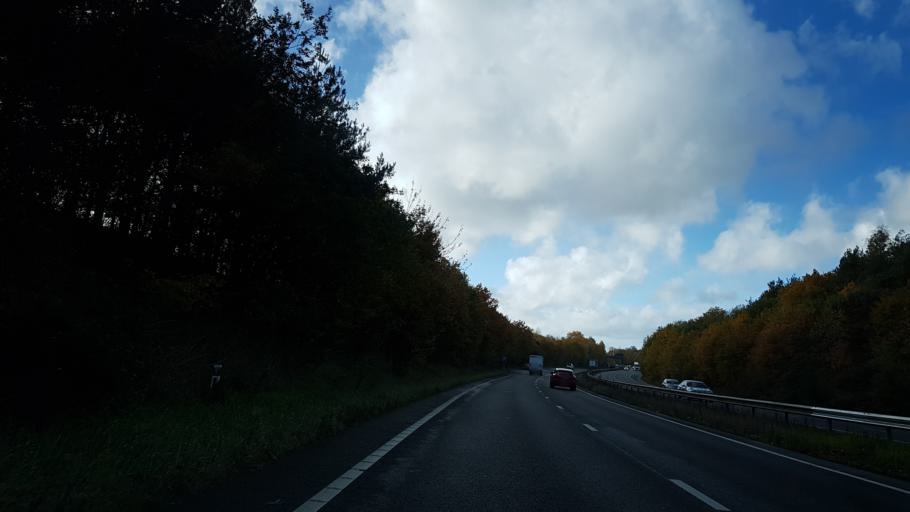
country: GB
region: England
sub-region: Surrey
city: Godalming
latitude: 51.2199
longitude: -0.6359
